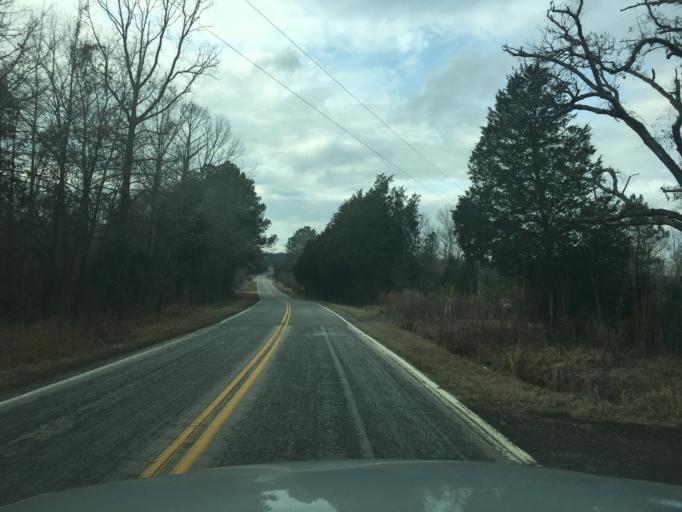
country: US
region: South Carolina
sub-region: Abbeville County
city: Due West
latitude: 34.2858
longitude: -82.4376
